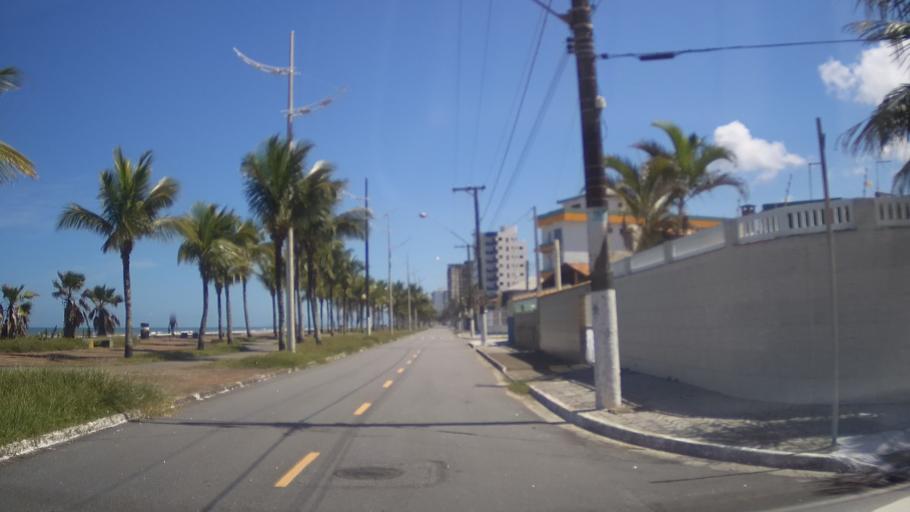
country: BR
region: Sao Paulo
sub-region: Mongagua
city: Mongagua
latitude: -24.0847
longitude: -46.5970
